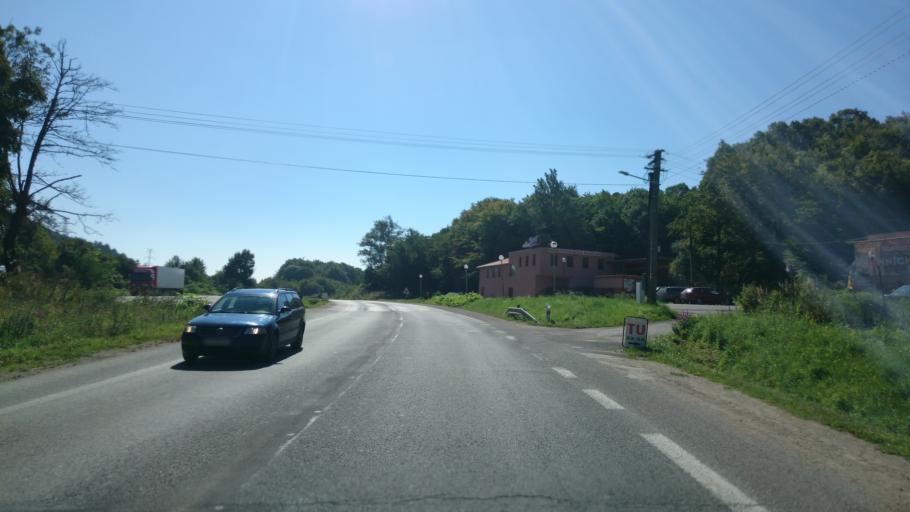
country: SK
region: Trenciansky
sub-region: Okres Trencin
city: Trencin
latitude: 48.8124
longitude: 18.0869
